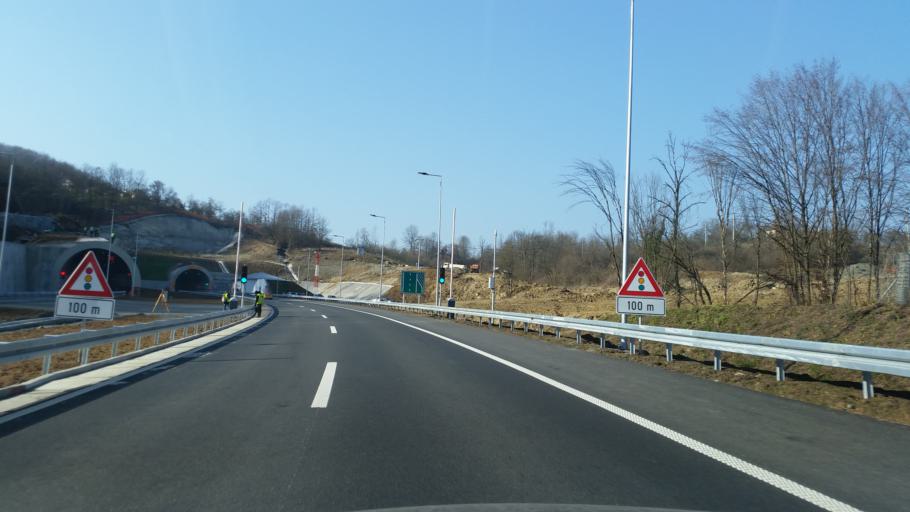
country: RS
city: Prislonica
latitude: 44.0124
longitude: 20.3808
